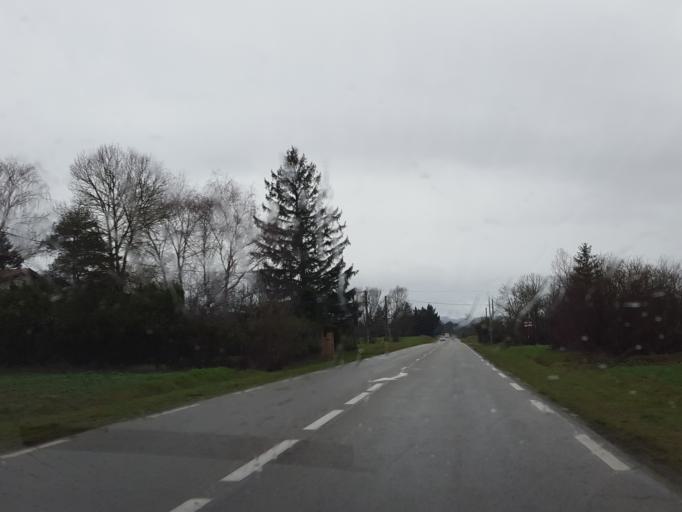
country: FR
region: Midi-Pyrenees
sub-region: Departement de l'Ariege
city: Mirepoix
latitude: 43.0850
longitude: 1.8543
